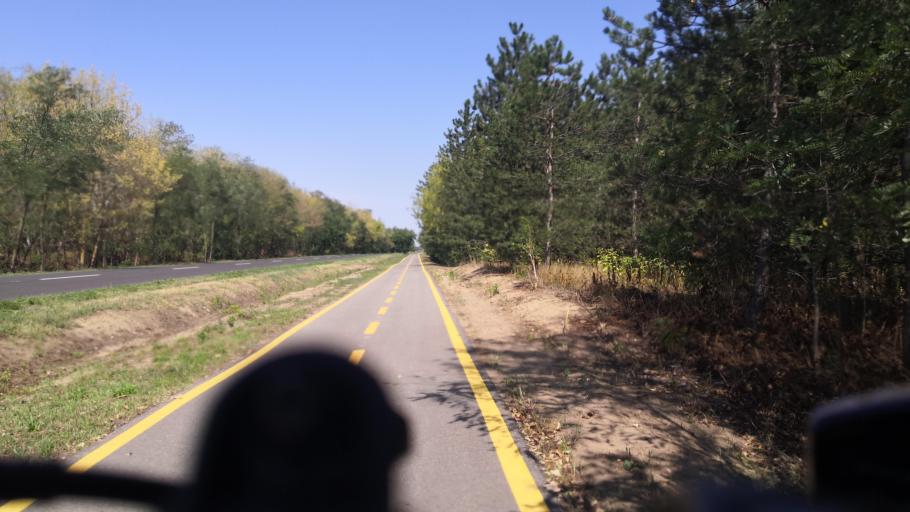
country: HU
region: Csongrad
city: Opusztaszer
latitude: 46.4599
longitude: 20.0964
